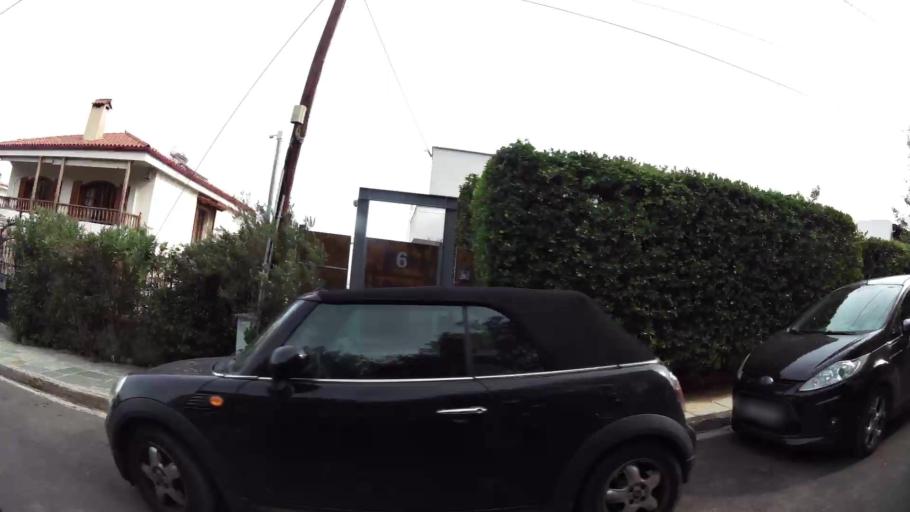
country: GR
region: Attica
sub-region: Nomarchia Athinas
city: Filothei
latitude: 38.0283
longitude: 23.7701
